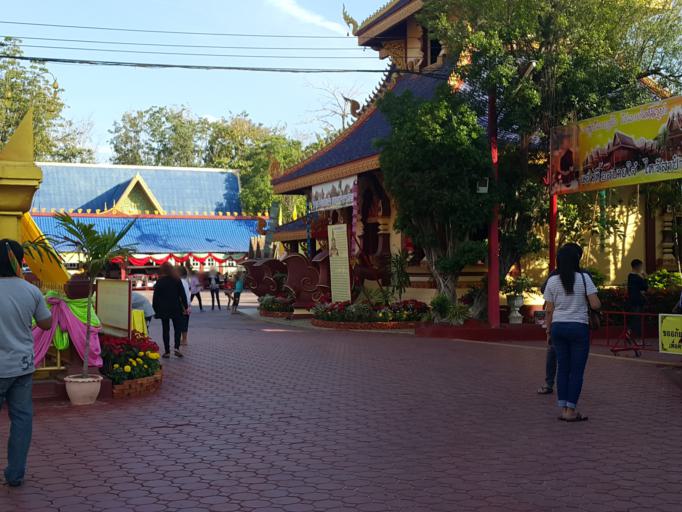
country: TH
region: Sukhothai
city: Thung Saliam
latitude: 17.3224
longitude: 99.5512
